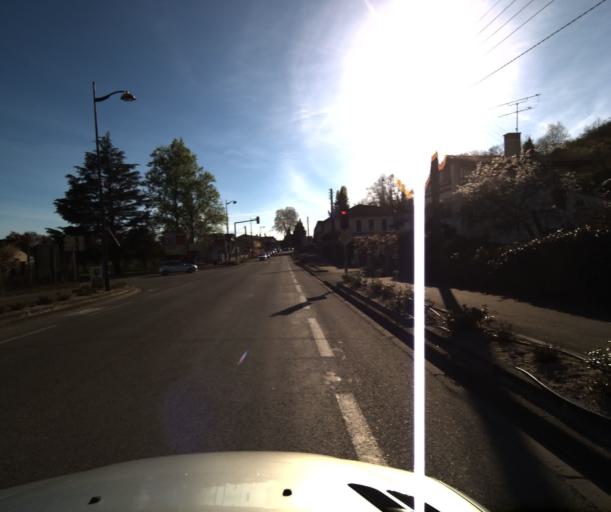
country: FR
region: Midi-Pyrenees
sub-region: Departement du Tarn-et-Garonne
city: Moissac
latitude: 44.1088
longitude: 1.1005
